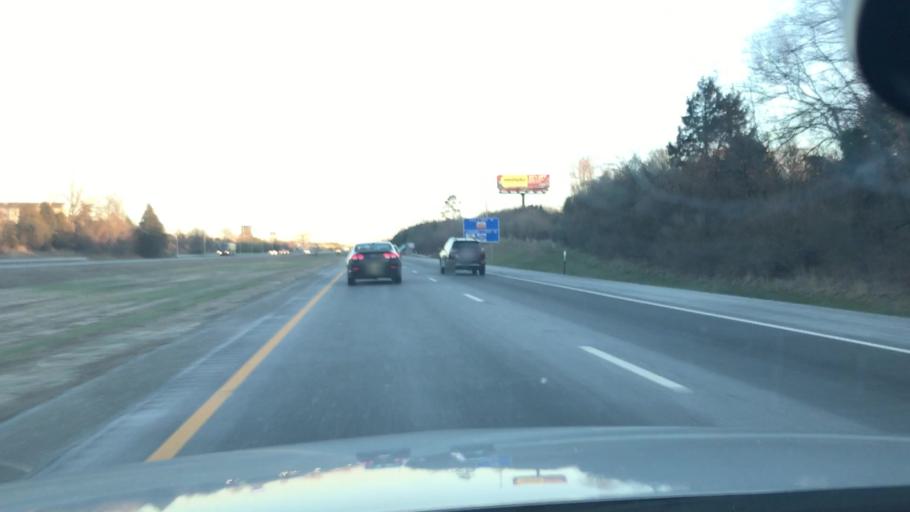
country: US
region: New Jersey
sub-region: Gloucester County
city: Turnersville
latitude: 39.7397
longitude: -75.0152
